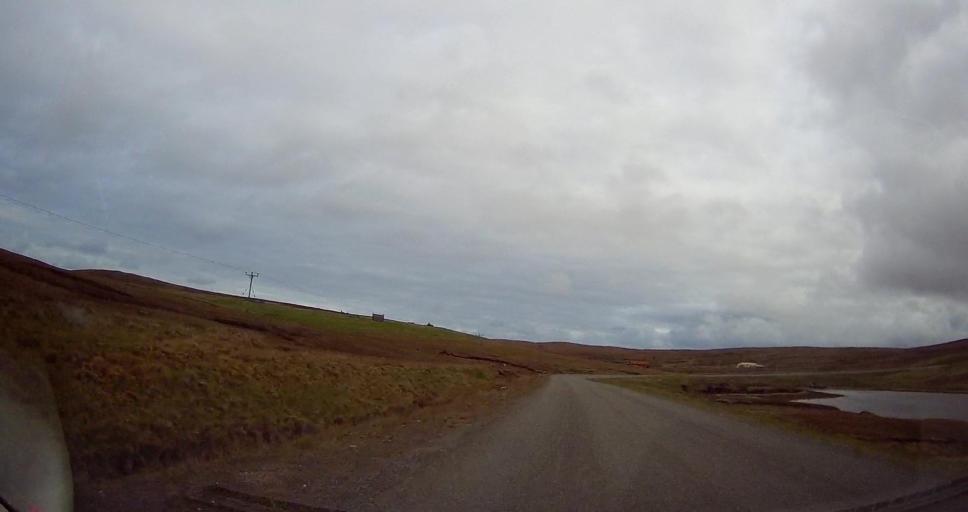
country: GB
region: Scotland
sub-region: Shetland Islands
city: Shetland
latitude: 60.6659
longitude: -1.0683
